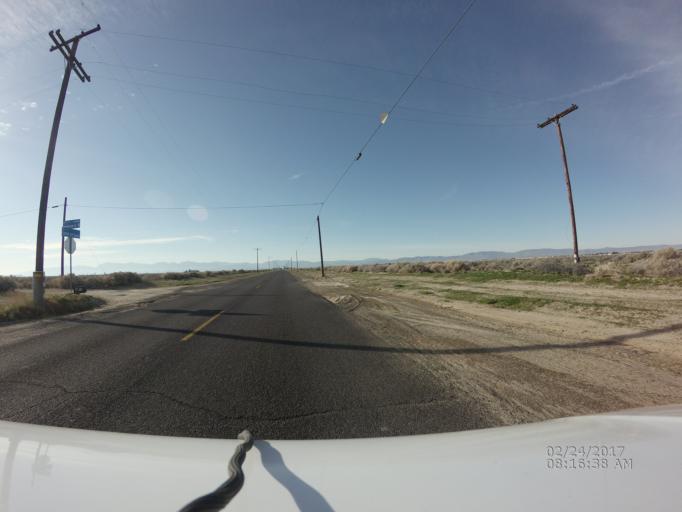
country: US
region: California
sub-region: Los Angeles County
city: Lancaster
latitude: 34.7266
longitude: -118.0412
